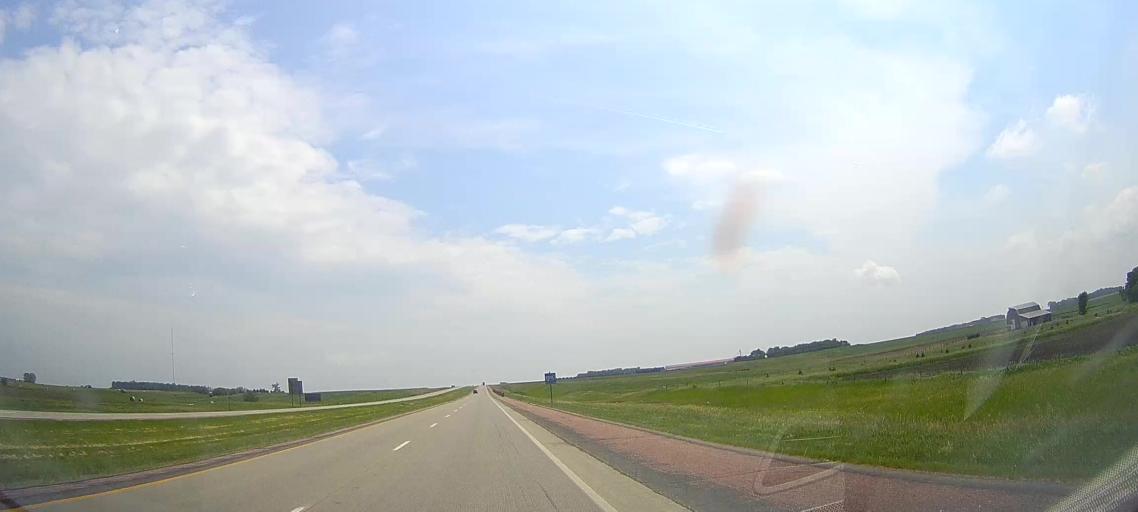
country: US
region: South Dakota
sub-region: Union County
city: Beresford
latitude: 43.0671
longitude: -96.7960
